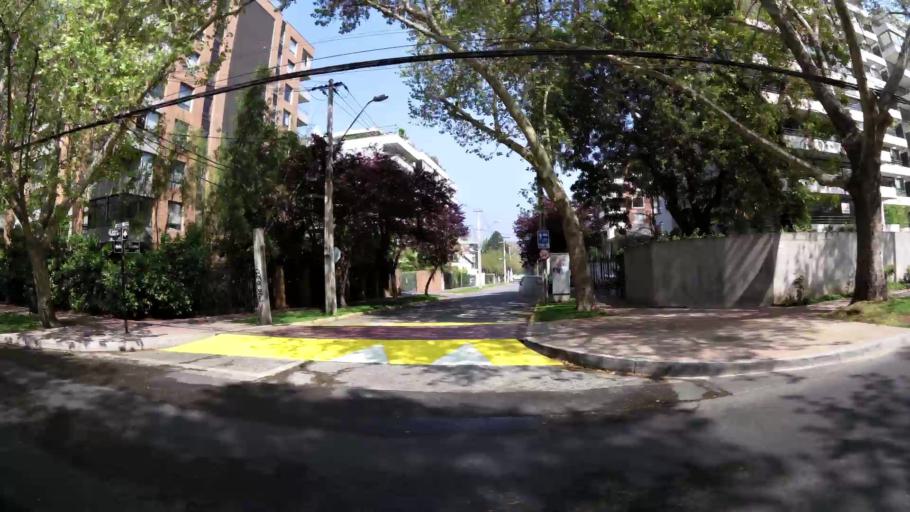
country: CL
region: Santiago Metropolitan
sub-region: Provincia de Santiago
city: Villa Presidente Frei, Nunoa, Santiago, Chile
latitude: -33.3962
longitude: -70.5894
